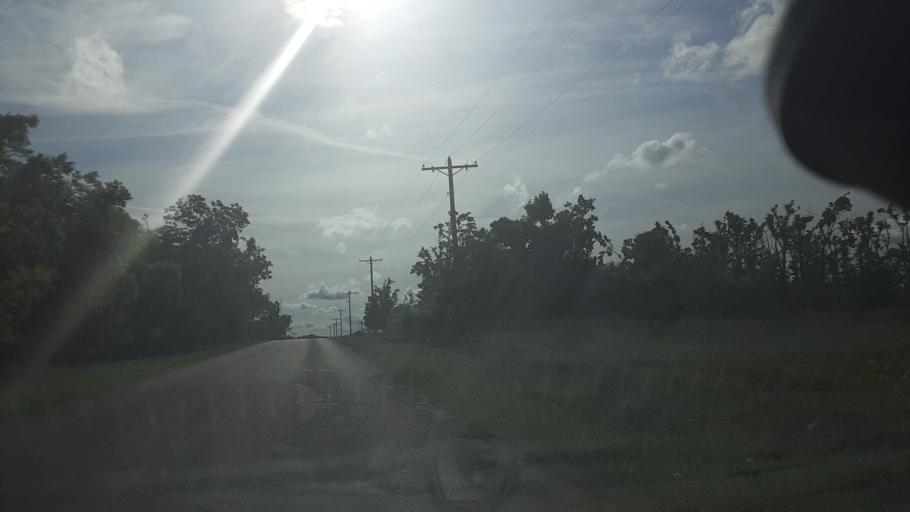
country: US
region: Oklahoma
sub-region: Logan County
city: Guthrie
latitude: 36.0576
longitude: -97.4046
